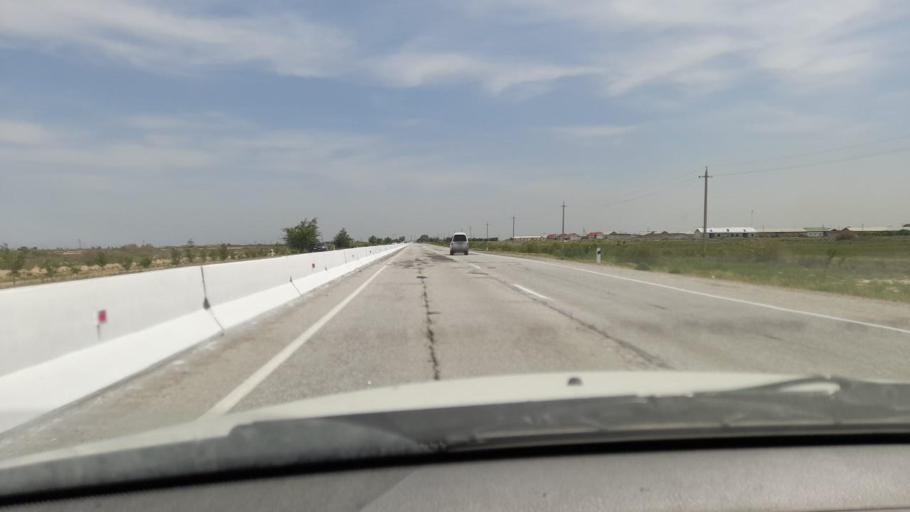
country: UZ
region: Navoiy
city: Konimex
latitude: 40.1090
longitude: 65.0545
